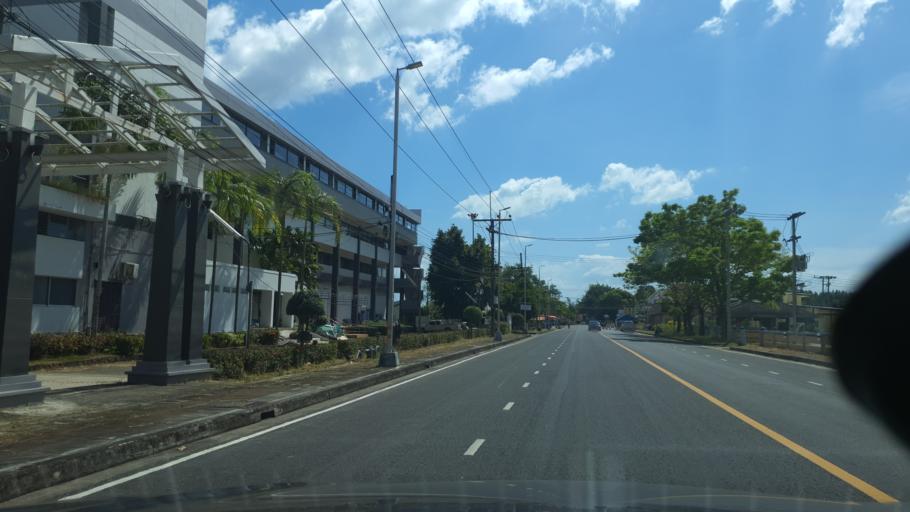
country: TH
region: Phangnga
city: Phang Nga
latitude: 8.3994
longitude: 98.5132
